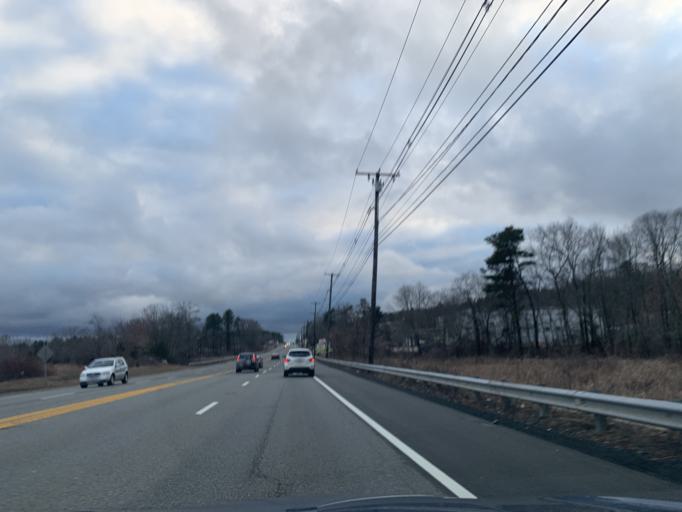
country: US
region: Massachusetts
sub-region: Norfolk County
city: Wrentham
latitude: 42.0529
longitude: -71.2996
